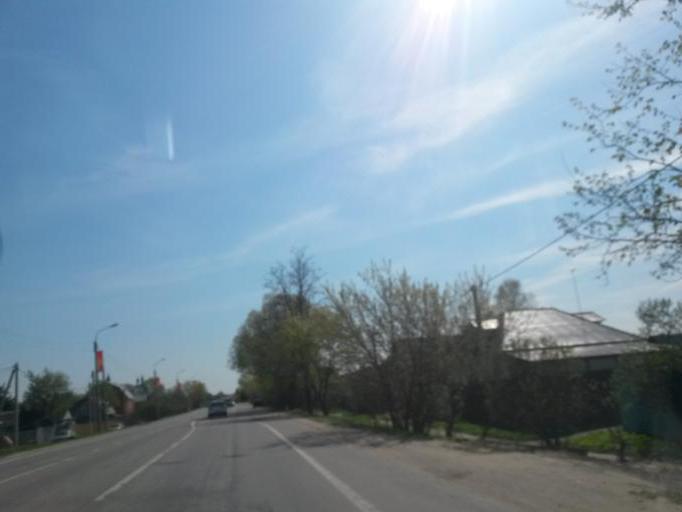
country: RU
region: Moskovskaya
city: Stolbovaya
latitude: 55.2791
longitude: 37.5101
